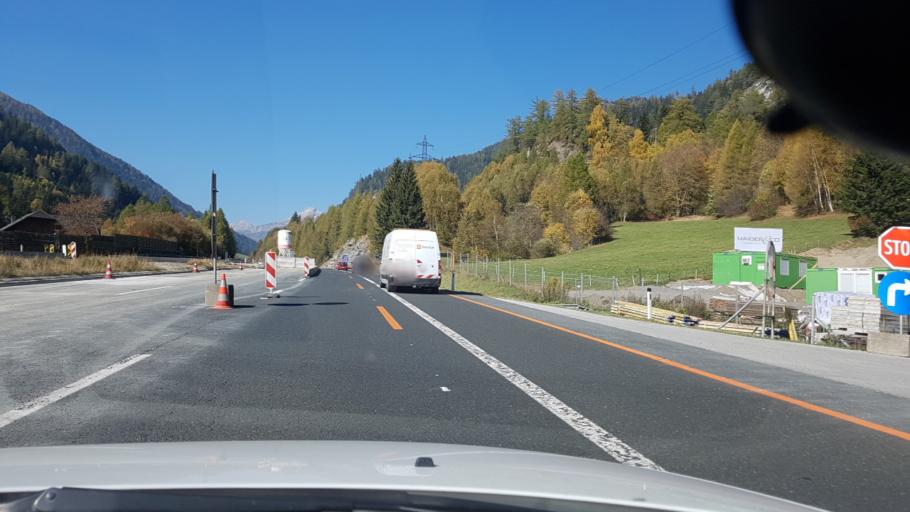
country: AT
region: Salzburg
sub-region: Politischer Bezirk Tamsweg
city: Zederhaus
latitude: 47.1353
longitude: 13.5434
